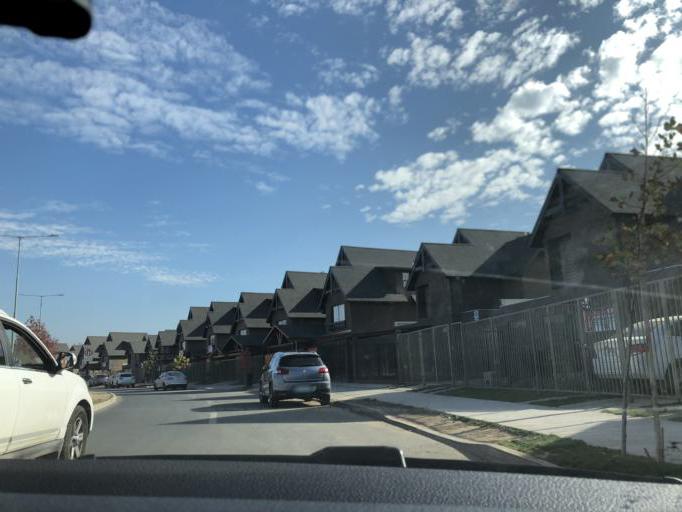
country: CL
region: Santiago Metropolitan
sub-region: Provincia de Cordillera
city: Puente Alto
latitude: -33.6009
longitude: -70.5163
